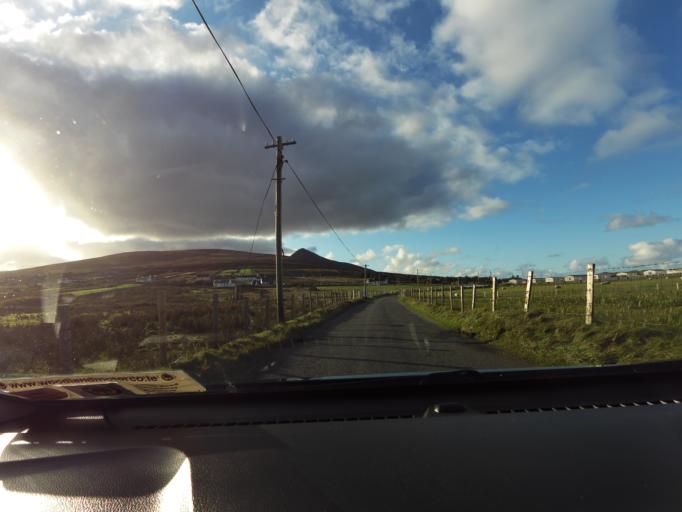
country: IE
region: Connaught
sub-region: Maigh Eo
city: Belmullet
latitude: 54.0096
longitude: -9.9893
